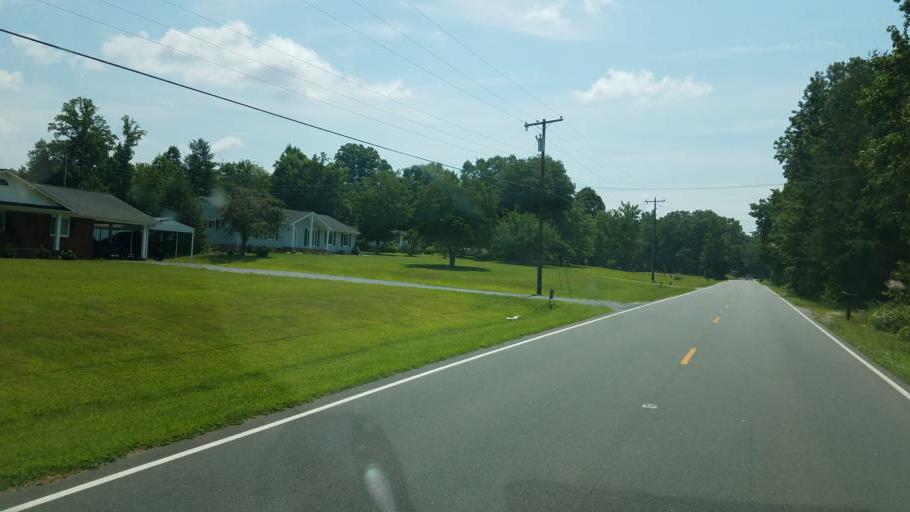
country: US
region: North Carolina
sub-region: Gaston County
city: Cherryville
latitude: 35.3615
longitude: -81.3622
